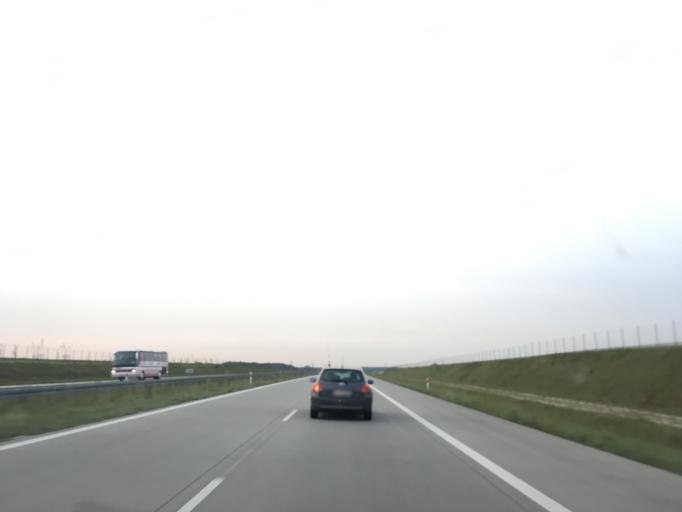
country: PL
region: Lodz Voivodeship
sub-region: Powiat lodzki wschodni
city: Tuszyn
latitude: 51.5963
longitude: 19.5837
